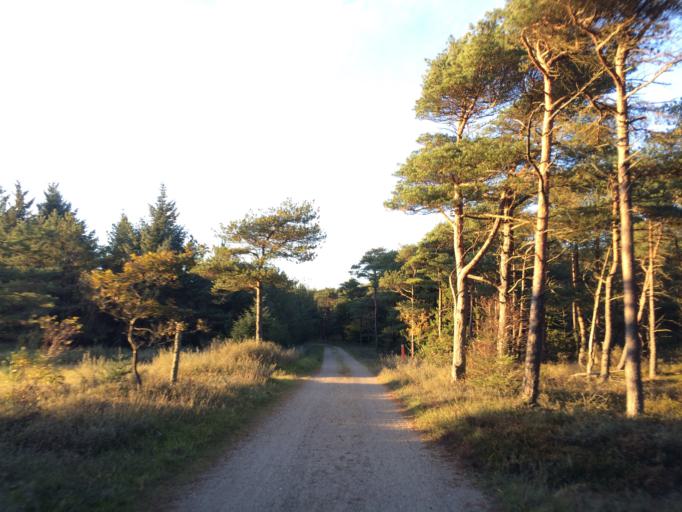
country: DK
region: Central Jutland
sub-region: Holstebro Kommune
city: Ulfborg
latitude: 56.2933
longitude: 8.1599
